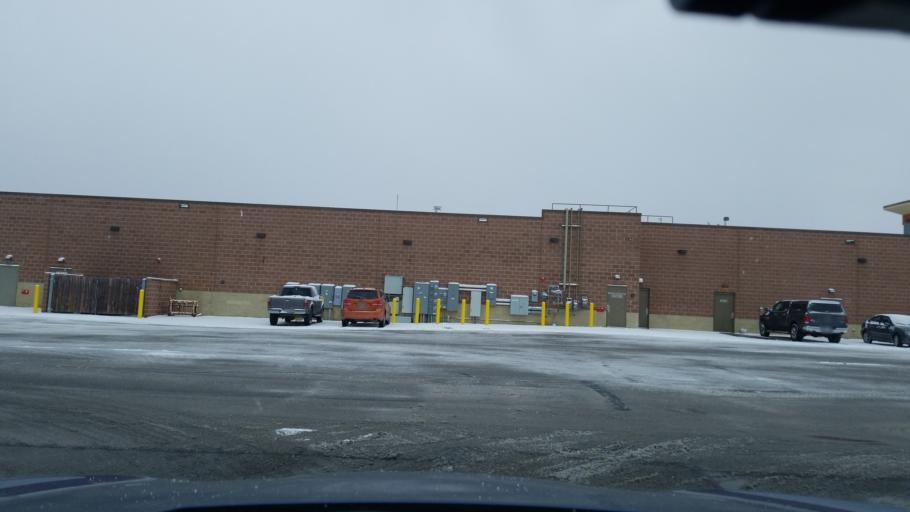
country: US
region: Ohio
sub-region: Cuyahoga County
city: Strongsville
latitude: 41.3148
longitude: -81.8183
